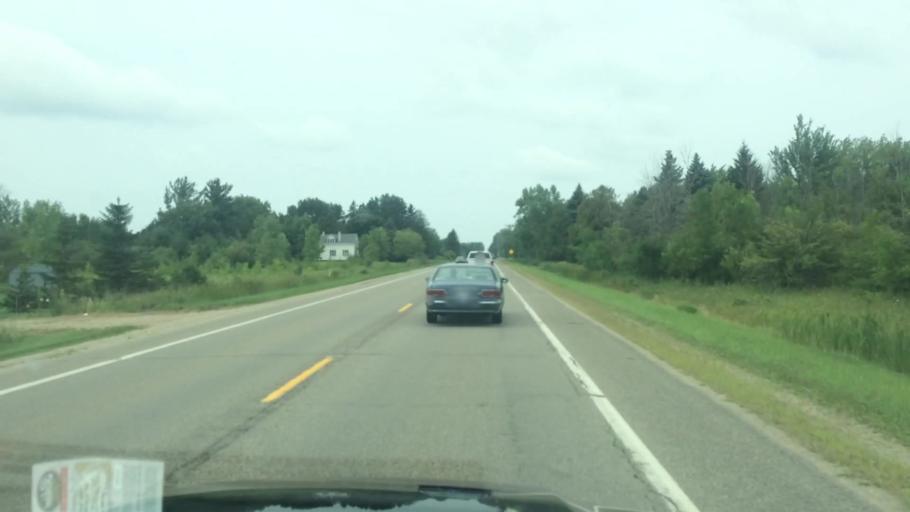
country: US
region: Michigan
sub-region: Huron County
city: Bad Axe
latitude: 43.8847
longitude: -83.0030
